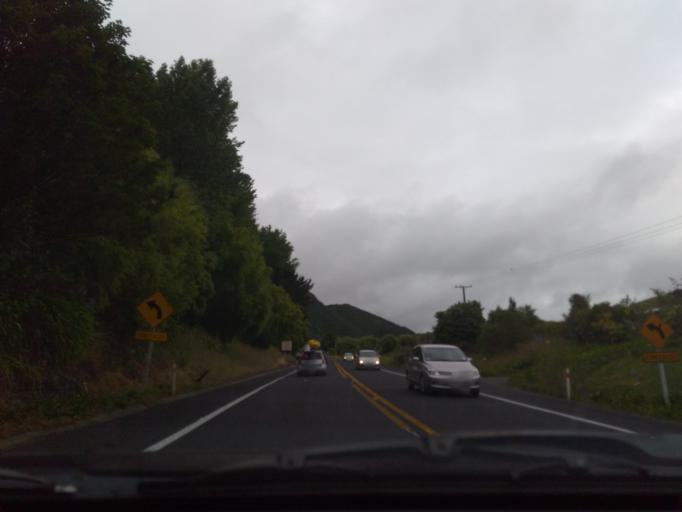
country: NZ
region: Auckland
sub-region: Auckland
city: Wellsford
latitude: -36.1243
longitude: 174.4330
